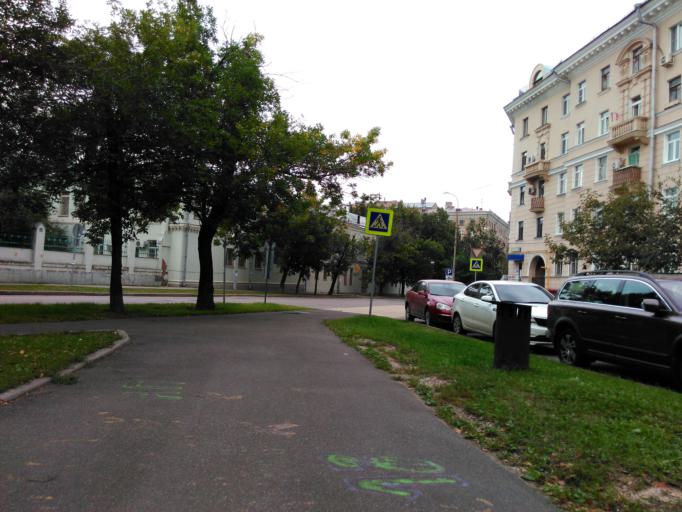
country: RU
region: Moscow
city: Novyye Cheremushki
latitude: 55.7150
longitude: 37.5947
